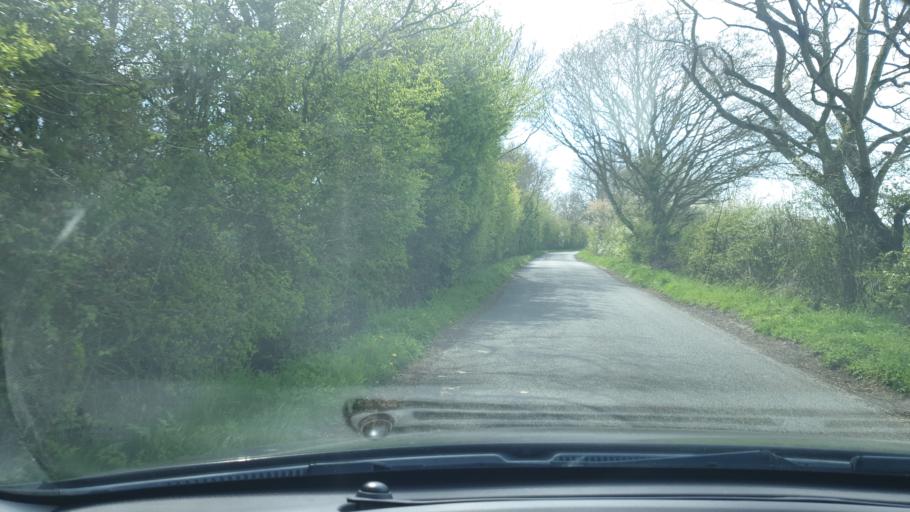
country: GB
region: England
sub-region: Essex
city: Mistley
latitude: 51.8969
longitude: 1.1008
